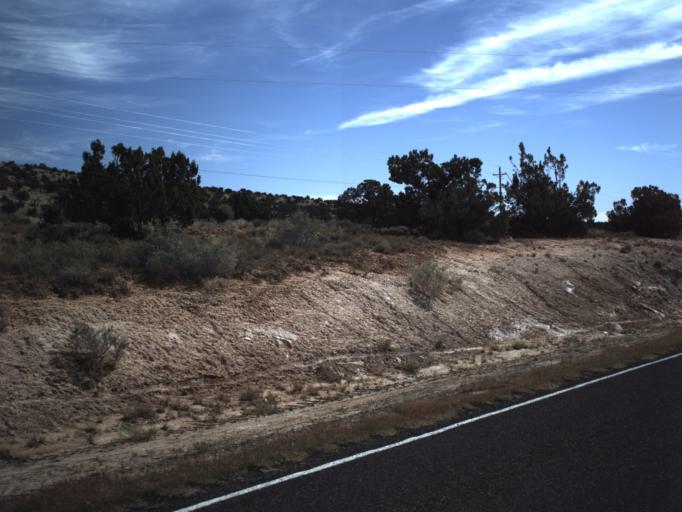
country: US
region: Utah
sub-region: Wayne County
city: Loa
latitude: 37.7477
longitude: -111.5641
